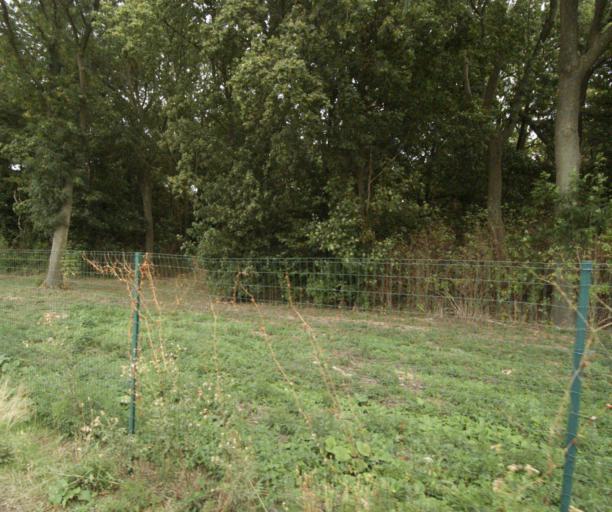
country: FR
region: Nord-Pas-de-Calais
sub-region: Departement du Nord
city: Lesquin
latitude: 50.5790
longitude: 3.1068
